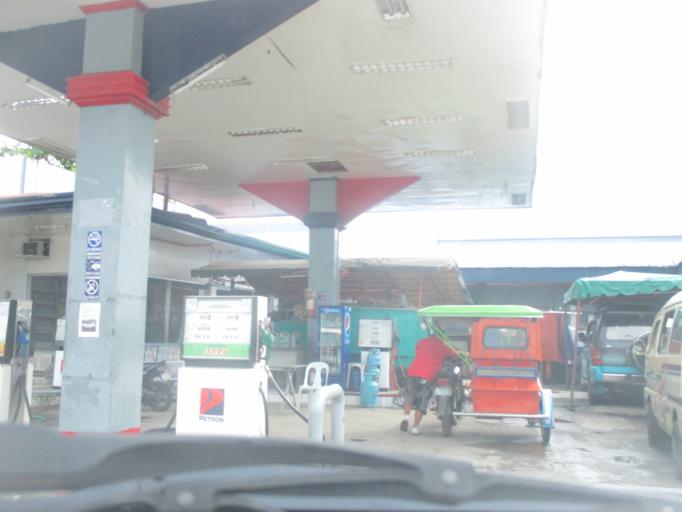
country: PH
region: Eastern Visayas
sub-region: Province of Leyte
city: Panalanoy
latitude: 11.2442
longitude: 124.9836
